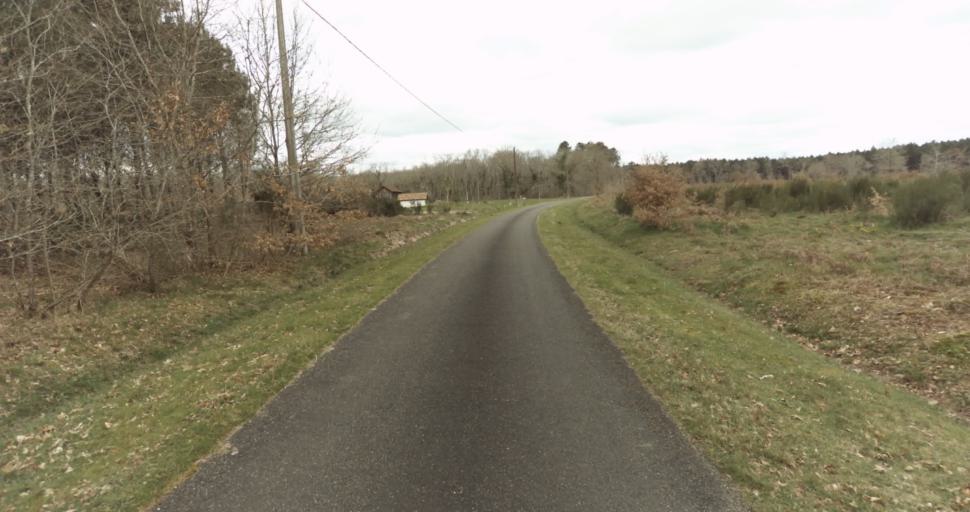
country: FR
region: Aquitaine
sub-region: Departement des Landes
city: Roquefort
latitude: 44.0727
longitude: -0.3824
